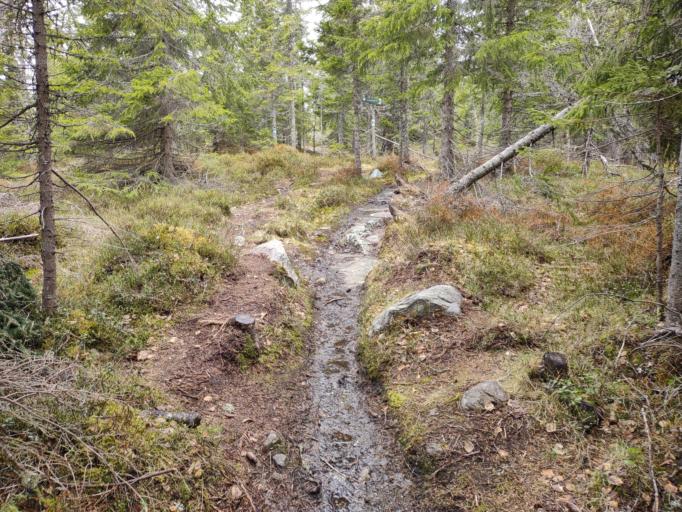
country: NO
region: Oppland
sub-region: Gran
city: Jaren
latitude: 60.4259
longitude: 10.6861
